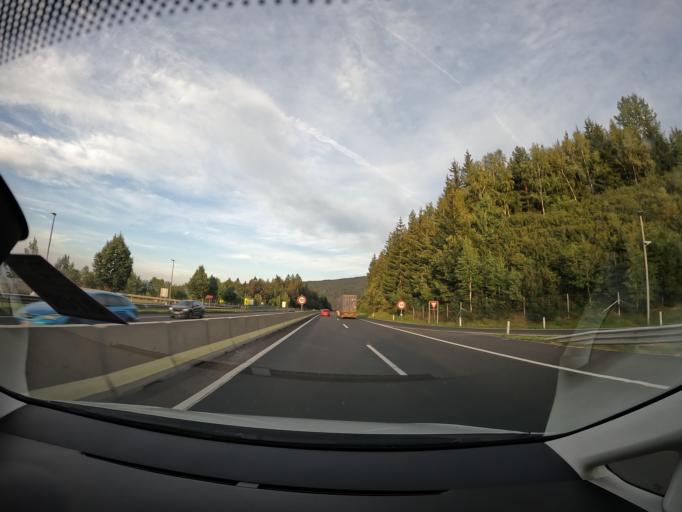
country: AT
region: Styria
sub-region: Politischer Bezirk Voitsberg
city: Voitsberg
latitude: 46.9898
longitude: 15.1123
